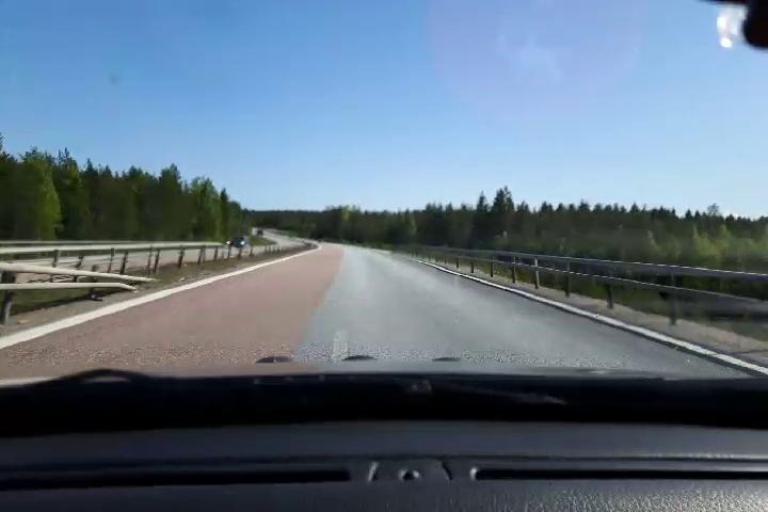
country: SE
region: Gaevleborg
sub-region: Soderhamns Kommun
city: Soderhamn
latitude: 61.3345
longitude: 17.0180
